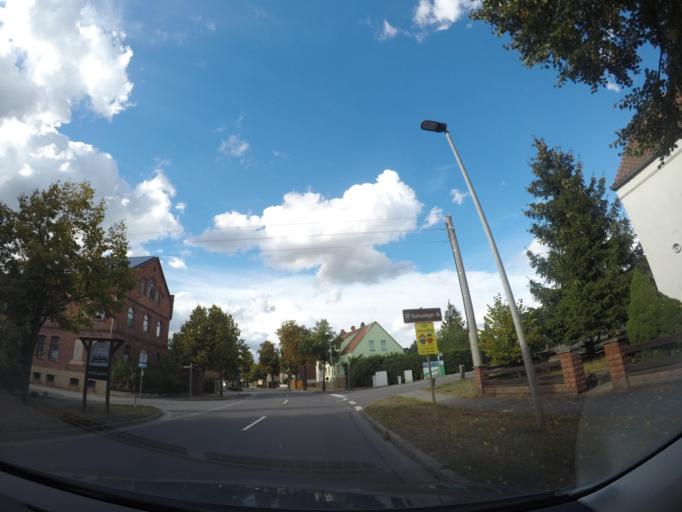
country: DE
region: Saxony-Anhalt
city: Bulstringen
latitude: 52.3198
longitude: 11.3479
